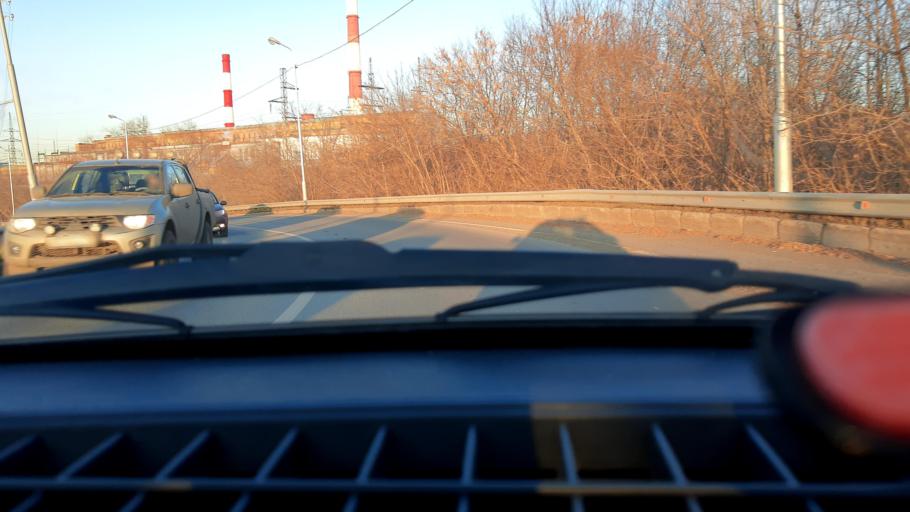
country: RU
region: Bashkortostan
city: Blagoveshchensk
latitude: 54.9085
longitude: 56.0657
